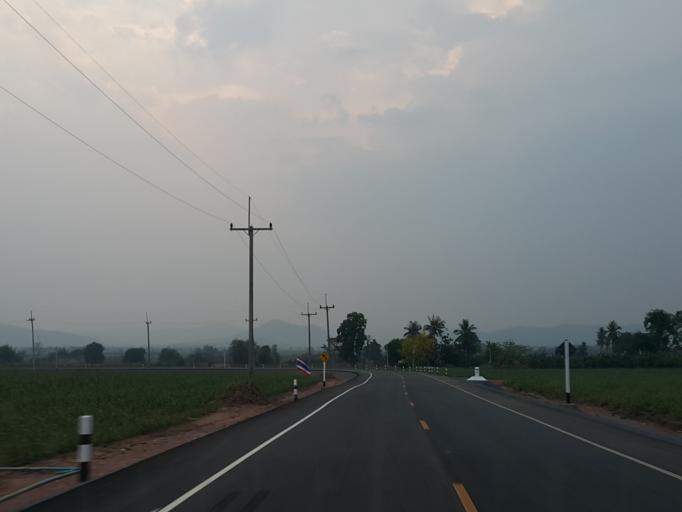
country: TH
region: Suphan Buri
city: Dan Chang
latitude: 14.9392
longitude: 99.6425
